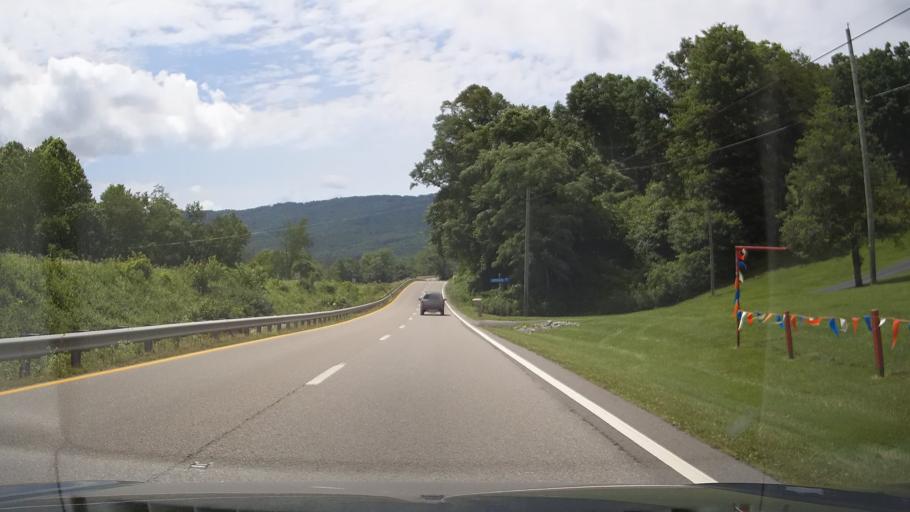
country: US
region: Virginia
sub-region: Lee County
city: Dryden
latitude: 36.7590
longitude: -82.8148
